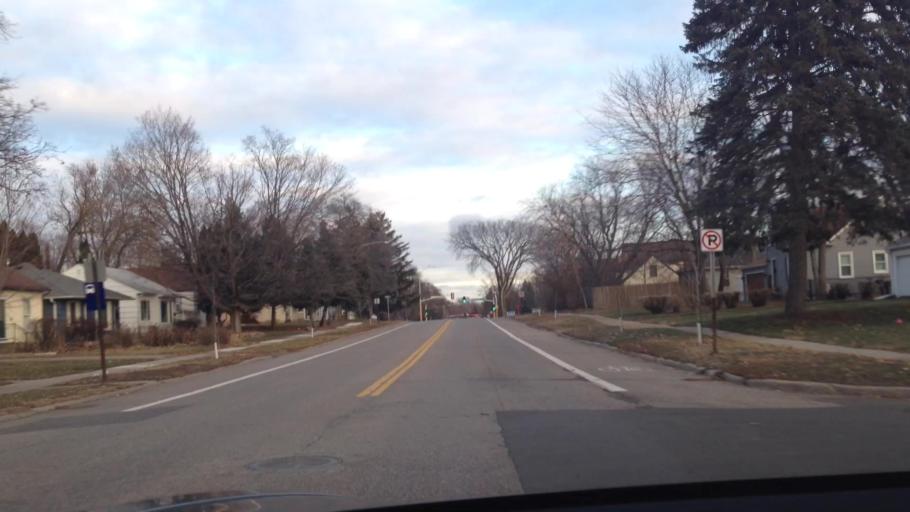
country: US
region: Minnesota
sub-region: Hennepin County
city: Saint Louis Park
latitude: 44.9496
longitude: -93.3683
